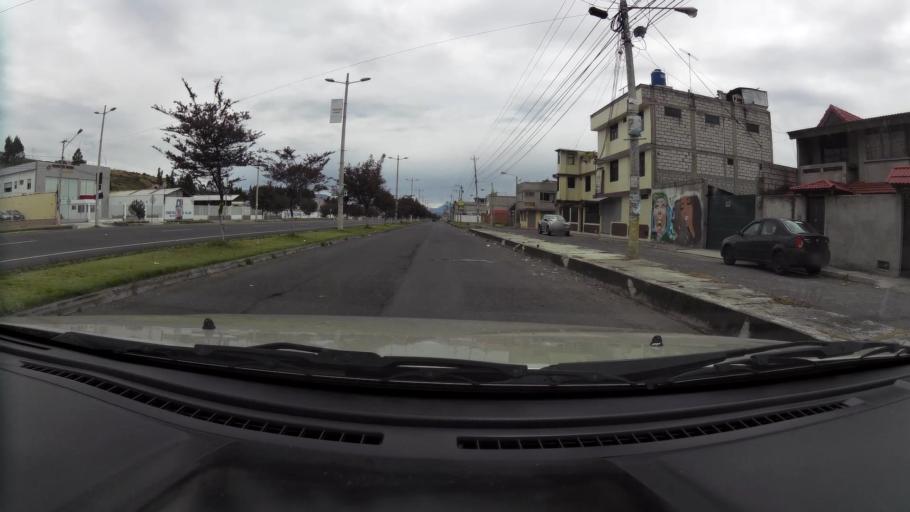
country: EC
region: Cotopaxi
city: Latacunga
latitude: -0.9605
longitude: -78.6120
